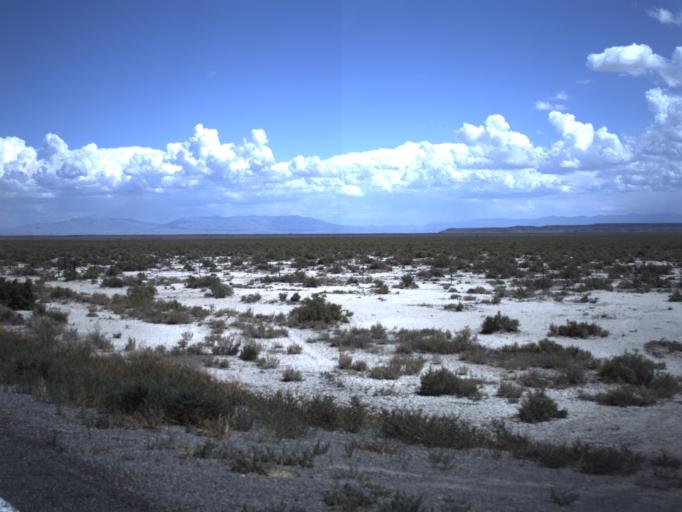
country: US
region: Utah
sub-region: Millard County
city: Delta
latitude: 39.2558
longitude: -112.8881
